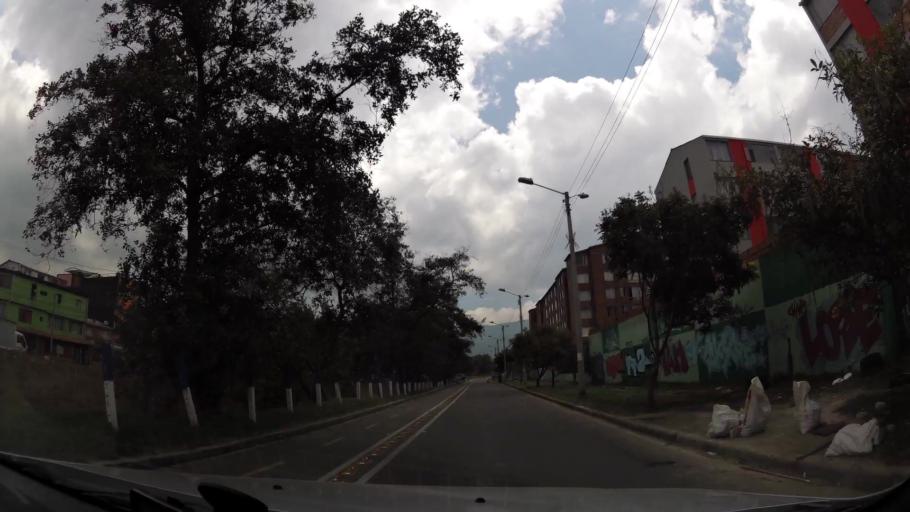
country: CO
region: Bogota D.C.
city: Bogota
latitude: 4.5934
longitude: -74.1025
